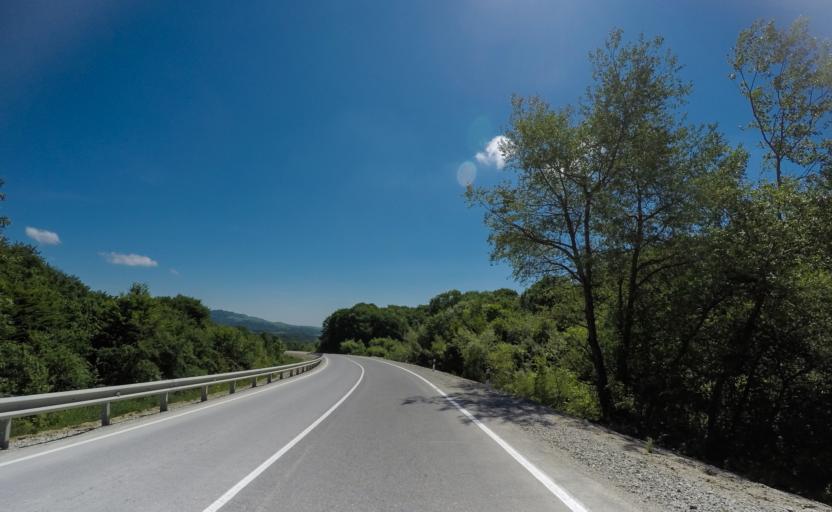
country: RU
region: Kabardino-Balkariya
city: Kashkhatau
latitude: 43.3716
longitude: 43.6150
